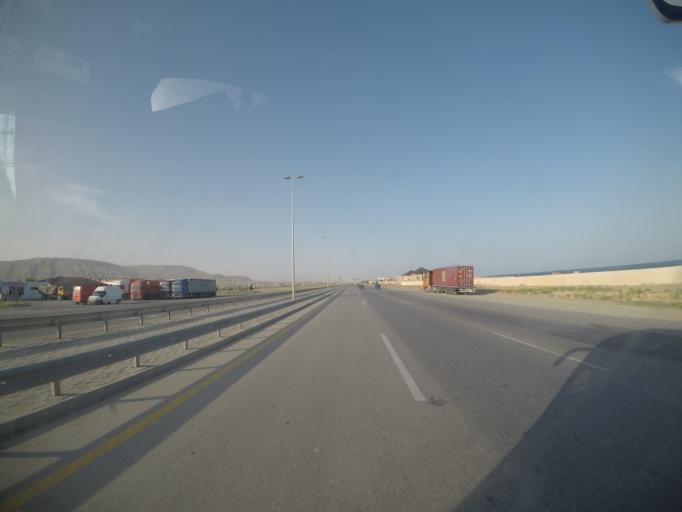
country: AZ
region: Baki
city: Qobustan
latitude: 40.1933
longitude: 49.5054
